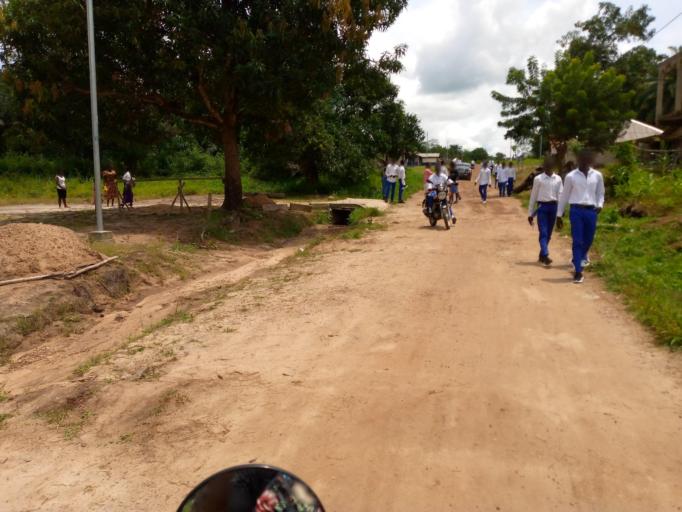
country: SL
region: Northern Province
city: Binkolo
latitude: 9.1097
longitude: -12.2032
